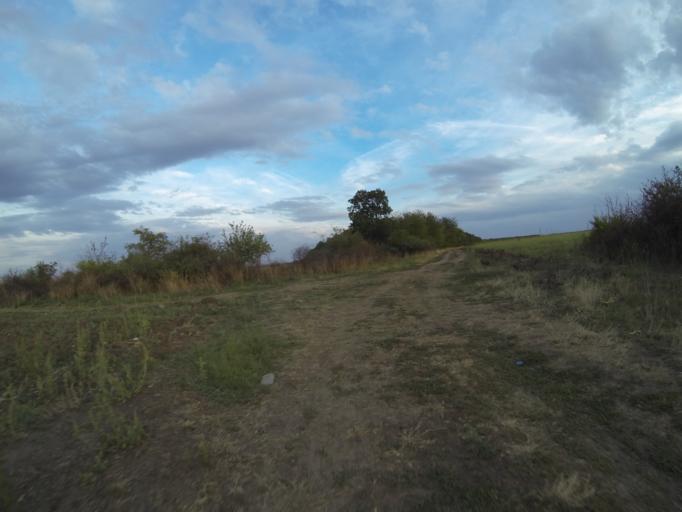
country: RO
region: Dolj
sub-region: Comuna Ceratu
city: Ceratu
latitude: 44.0941
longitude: 23.6715
